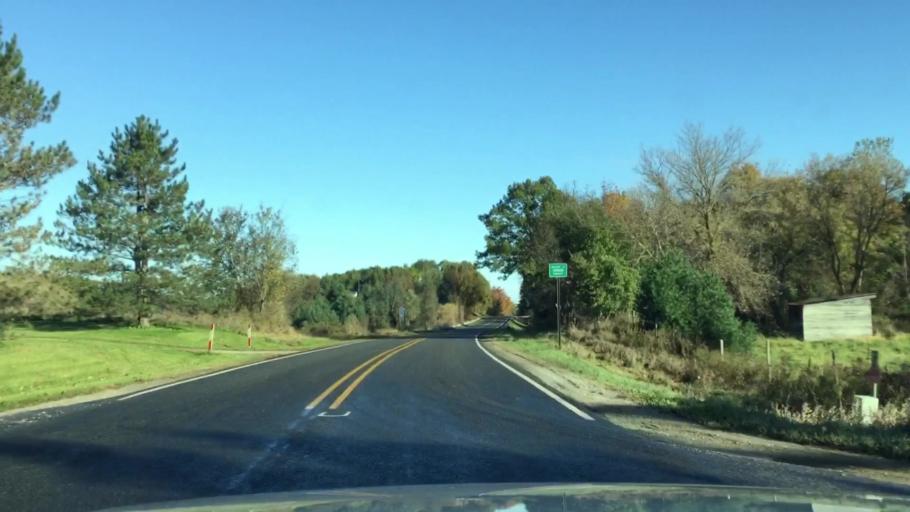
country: US
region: Michigan
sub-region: Shiawassee County
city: Durand
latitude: 42.8681
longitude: -83.9468
